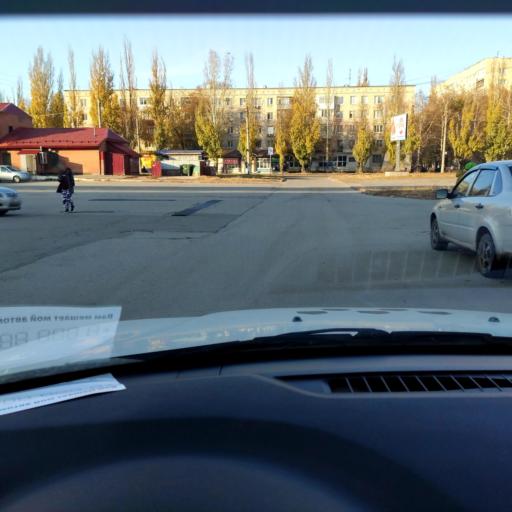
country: RU
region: Samara
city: Tol'yatti
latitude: 53.5108
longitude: 49.4457
